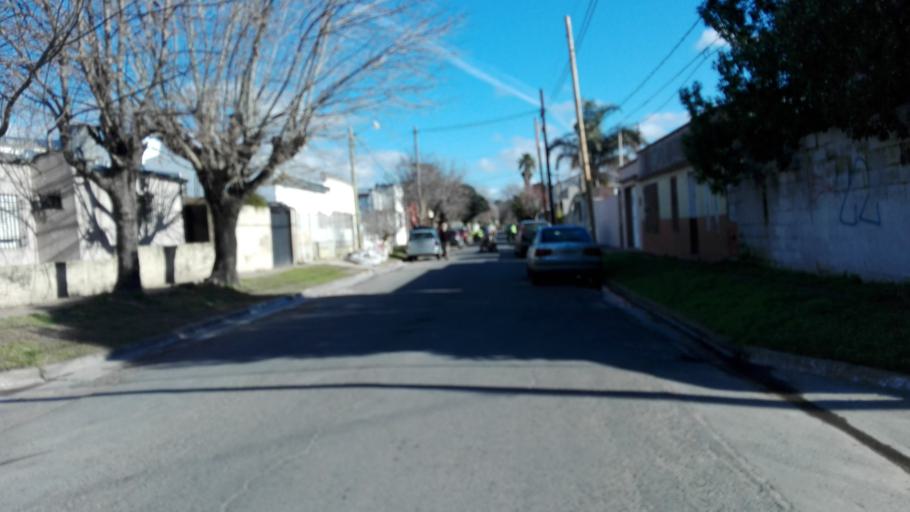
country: AR
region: Buenos Aires
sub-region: Partido de La Plata
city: La Plata
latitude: -34.8835
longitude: -57.9953
